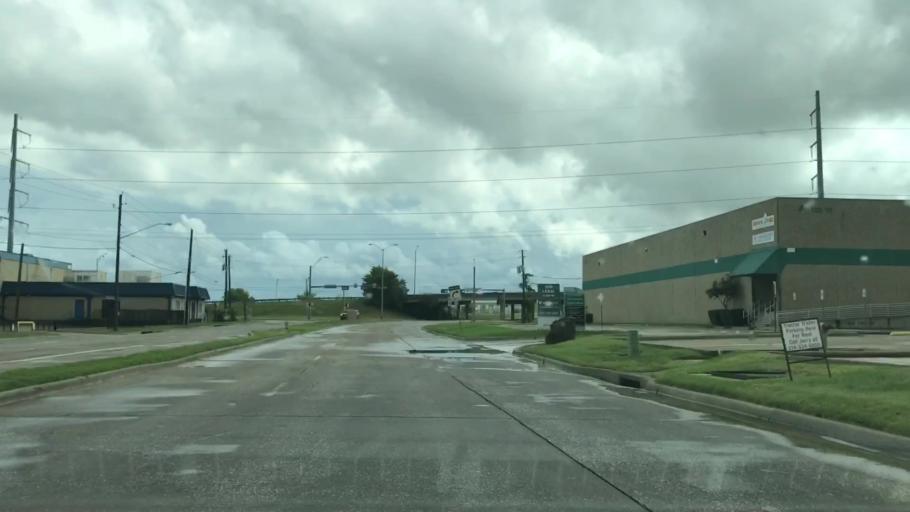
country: US
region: Texas
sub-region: Dallas County
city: Irving
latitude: 32.8103
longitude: -96.9003
